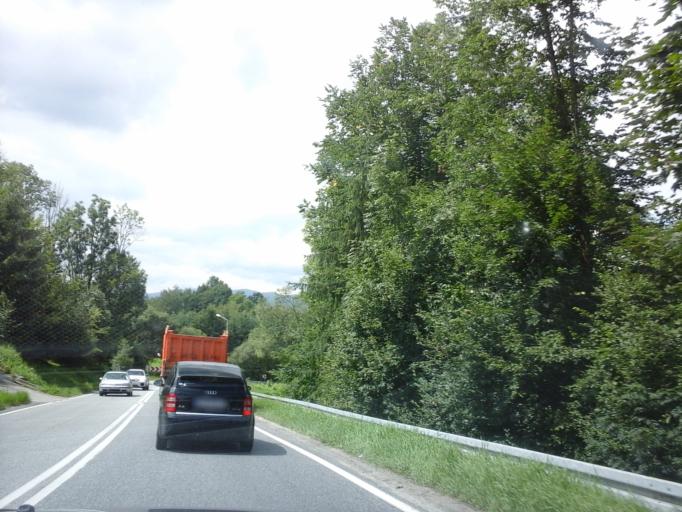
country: PL
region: Lesser Poland Voivodeship
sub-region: Powiat suski
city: Jordanow
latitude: 49.6512
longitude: 19.8263
